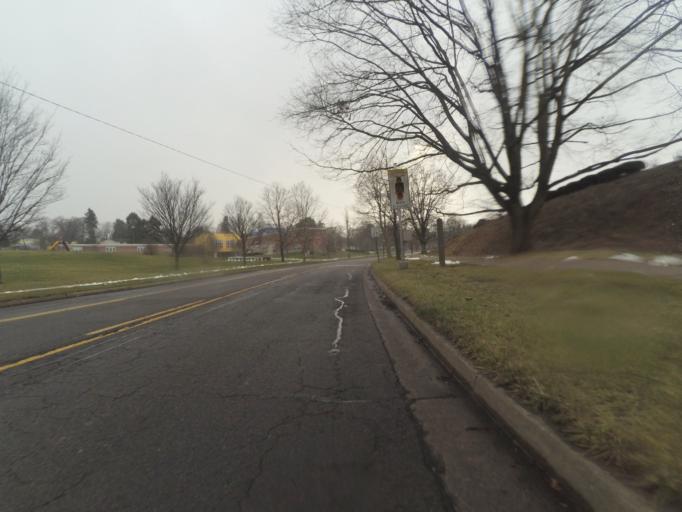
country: US
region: Pennsylvania
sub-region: Centre County
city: State College
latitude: 40.7901
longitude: -77.8474
